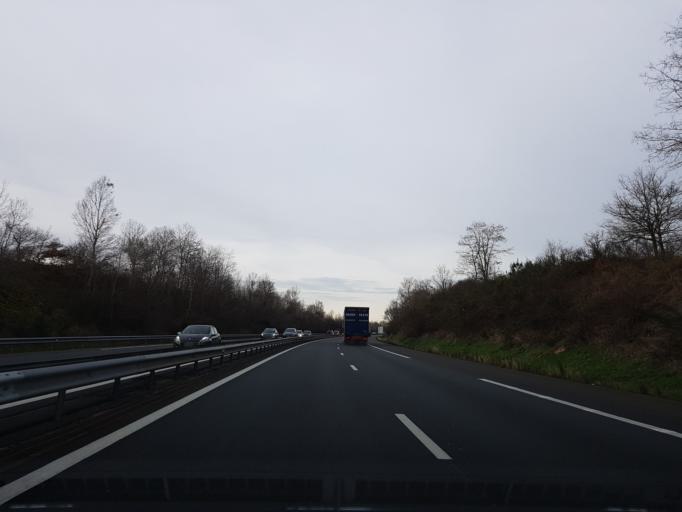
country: FR
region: Auvergne
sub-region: Departement de l'Allier
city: Montmarault
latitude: 46.3330
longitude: 2.8925
